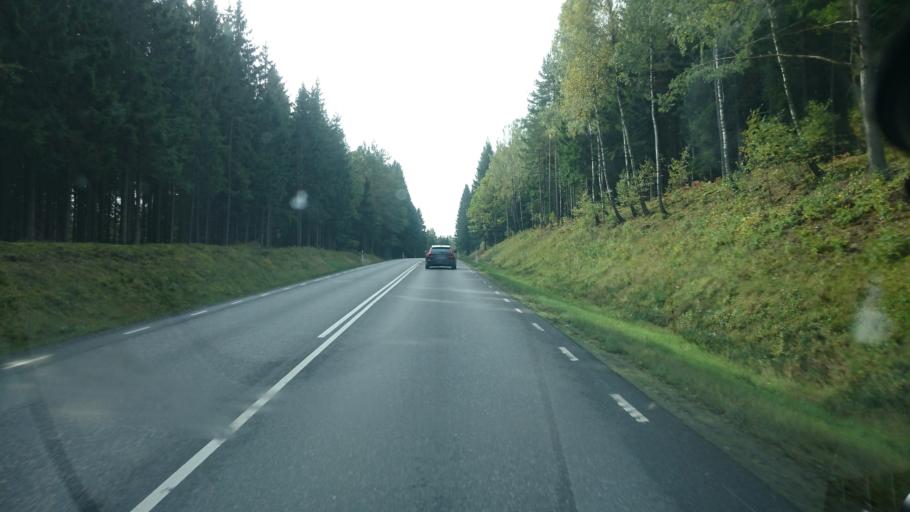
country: SE
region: Vaestra Goetaland
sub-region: Alingsas Kommun
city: Sollebrunn
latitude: 58.0285
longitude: 12.4620
